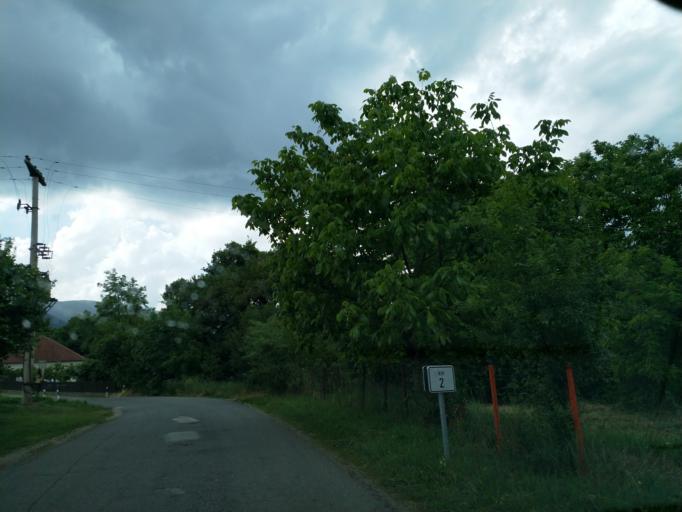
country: RS
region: Central Serbia
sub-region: Borski Okrug
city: Bor
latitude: 44.0261
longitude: 21.9762
